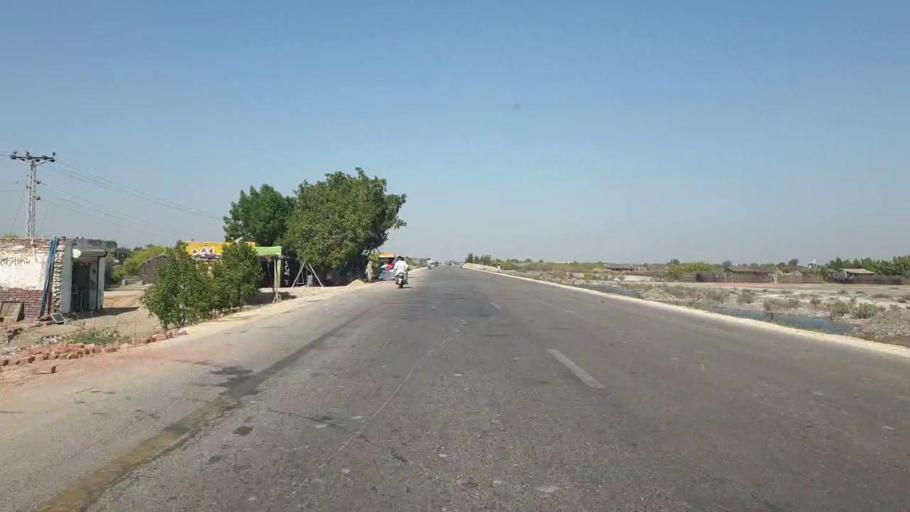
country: PK
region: Sindh
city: Talhar
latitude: 24.8479
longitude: 68.8163
